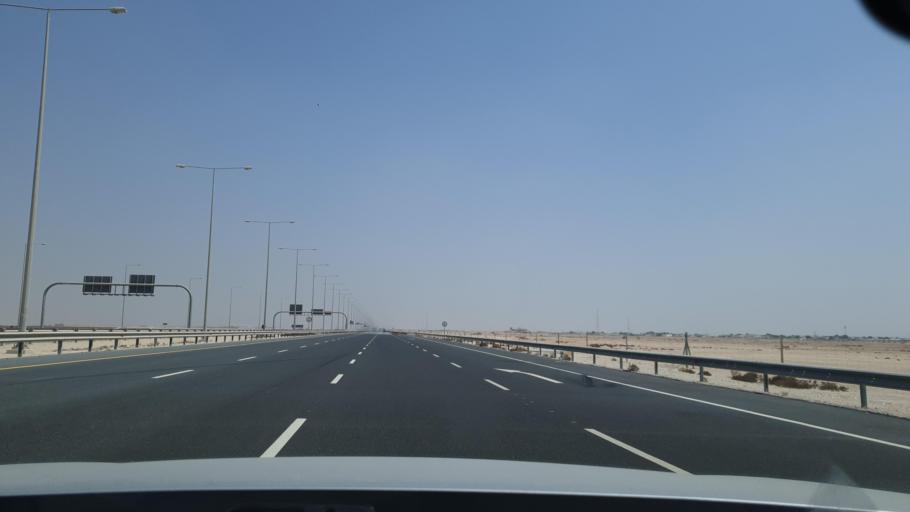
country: QA
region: Baladiyat az Za`ayin
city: Az Za`ayin
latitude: 25.6181
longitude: 51.3765
